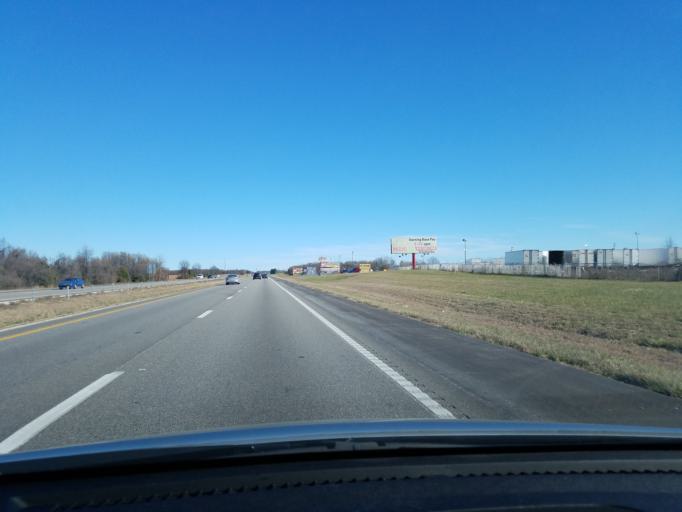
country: US
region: Missouri
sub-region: Greene County
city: Strafford
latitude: 37.2561
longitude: -93.1657
